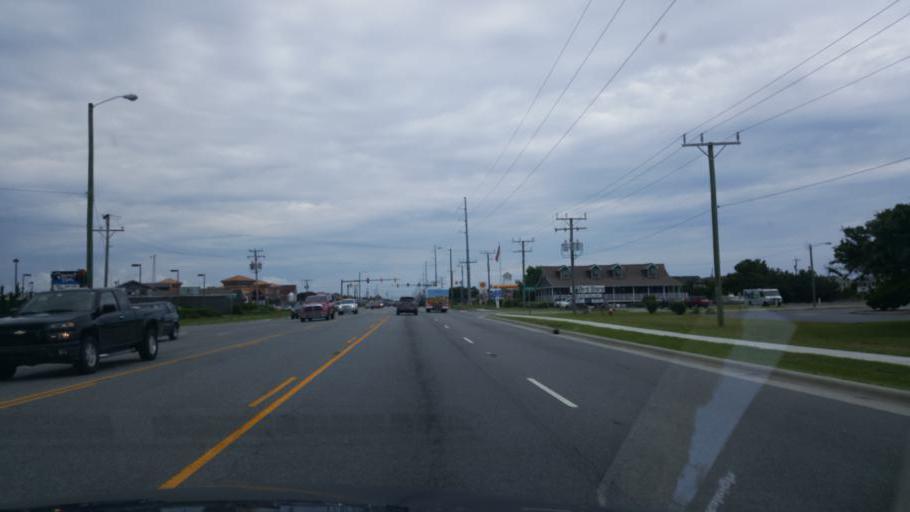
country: US
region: North Carolina
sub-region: Dare County
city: Kill Devil Hills
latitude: 36.0072
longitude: -75.6570
